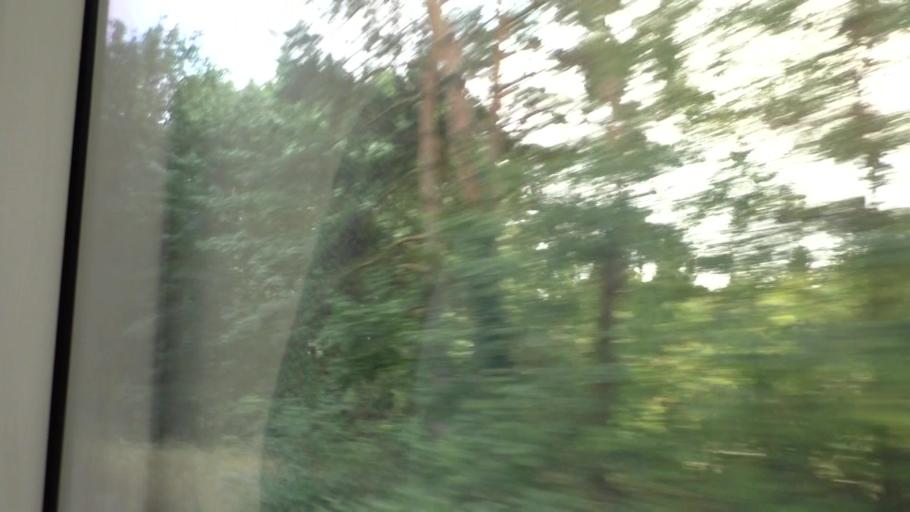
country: DE
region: Brandenburg
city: Konigs Wusterhausen
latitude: 52.2983
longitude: 13.6778
